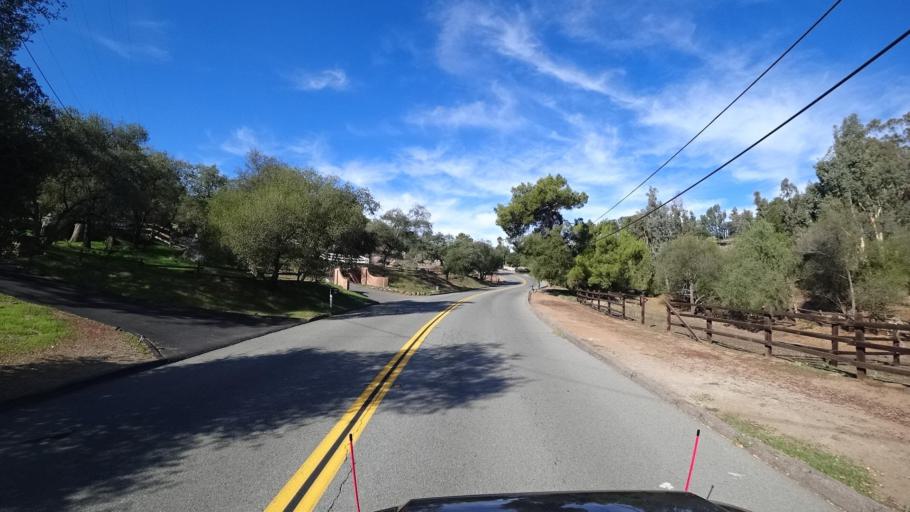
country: US
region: California
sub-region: San Diego County
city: Alpine
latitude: 32.8201
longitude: -116.7542
